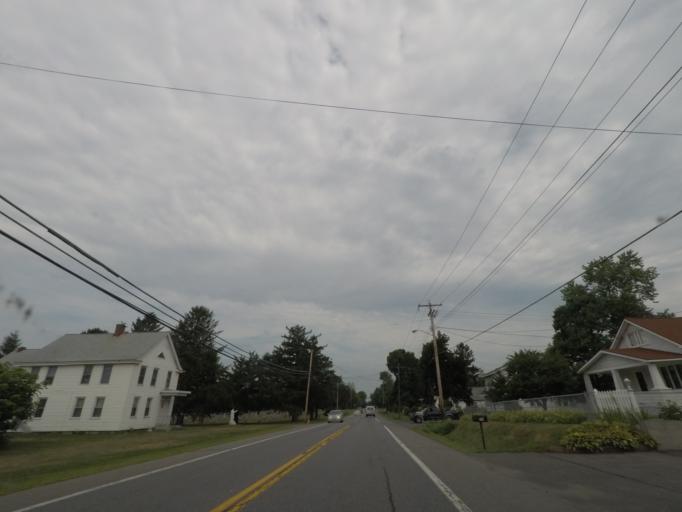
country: US
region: New York
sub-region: Saratoga County
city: Waterford
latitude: 42.7994
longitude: -73.6813
